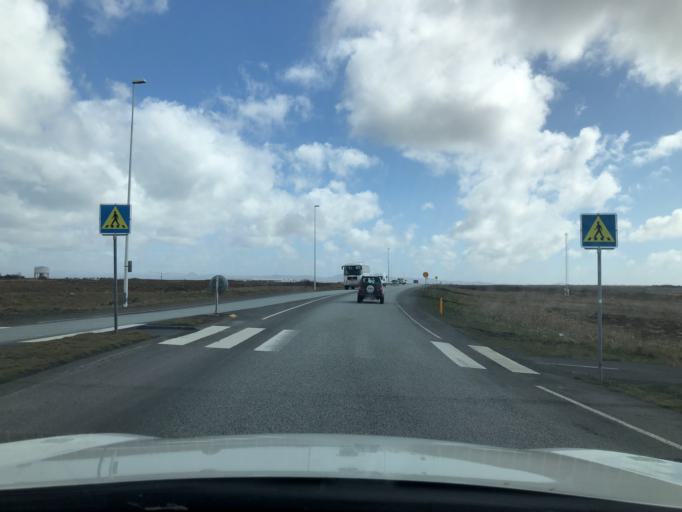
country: IS
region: Southern Peninsula
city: Reykjanesbaer
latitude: 64.0026
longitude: -22.6024
